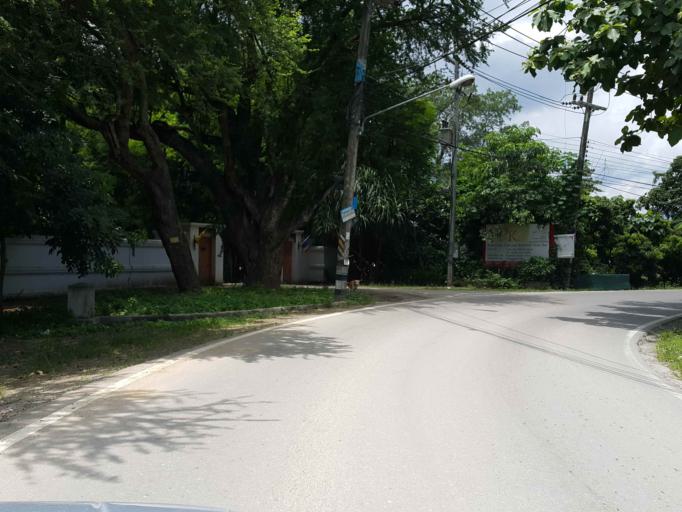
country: TH
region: Chiang Mai
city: San Sai
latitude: 18.8574
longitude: 98.9855
